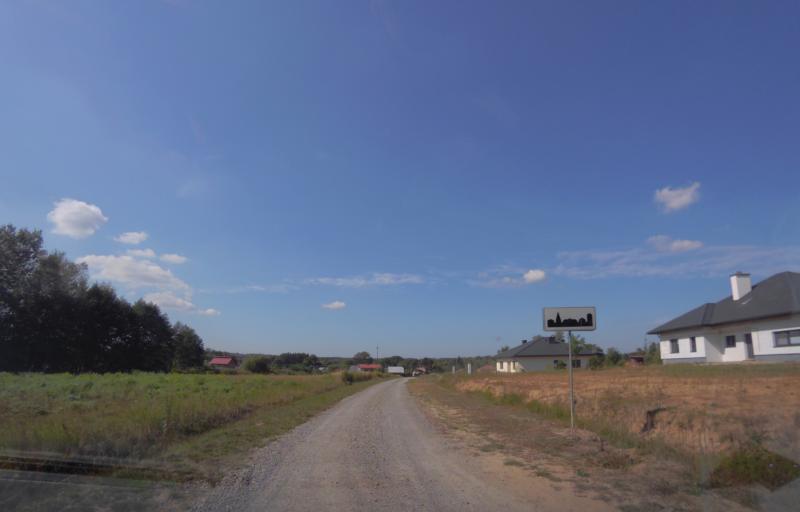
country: PL
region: Subcarpathian Voivodeship
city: Nowa Sarzyna
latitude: 50.2991
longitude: 22.3150
